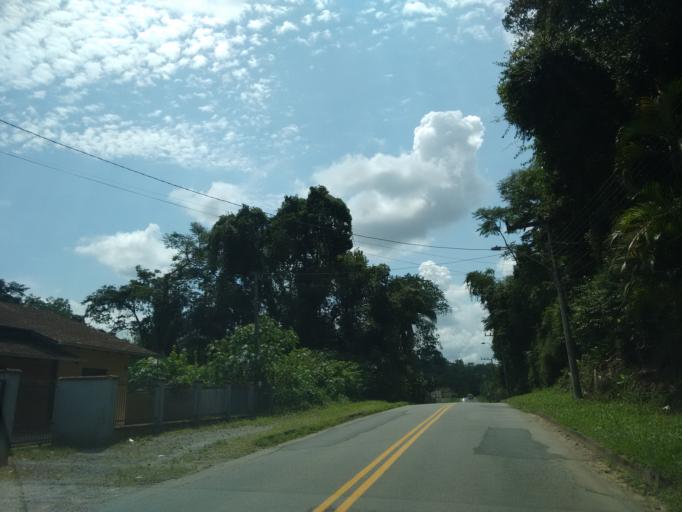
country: BR
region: Santa Catarina
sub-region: Blumenau
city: Blumenau
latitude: -26.8638
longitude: -49.1385
